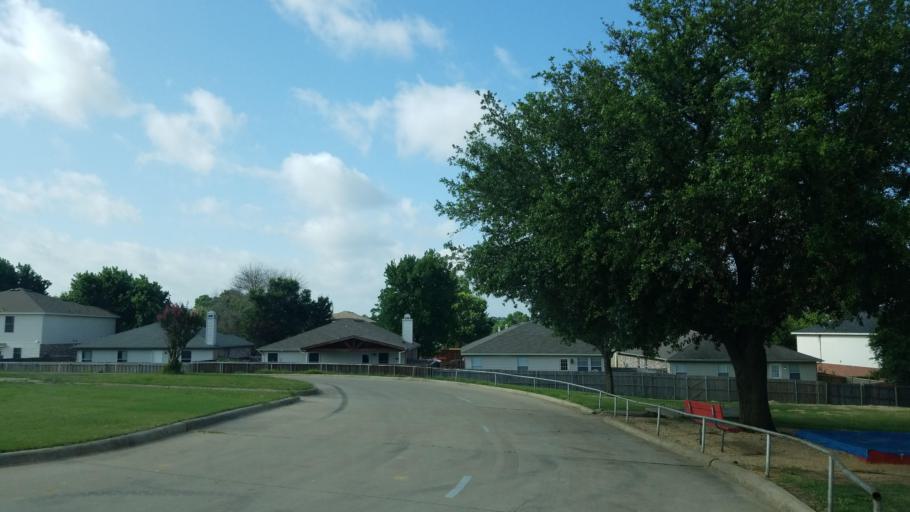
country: US
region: Texas
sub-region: Denton County
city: Copper Canyon
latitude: 33.1456
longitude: -97.1215
